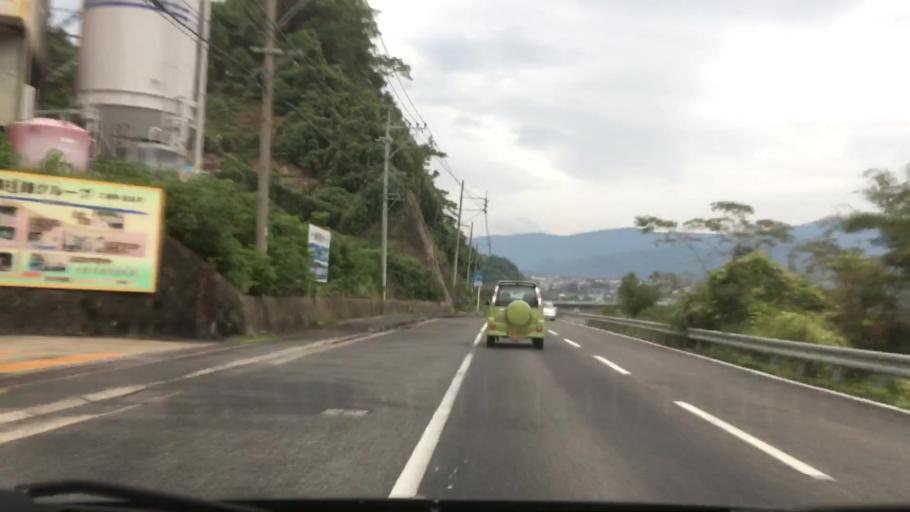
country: JP
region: Nagasaki
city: Sasebo
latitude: 33.1219
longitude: 129.7936
